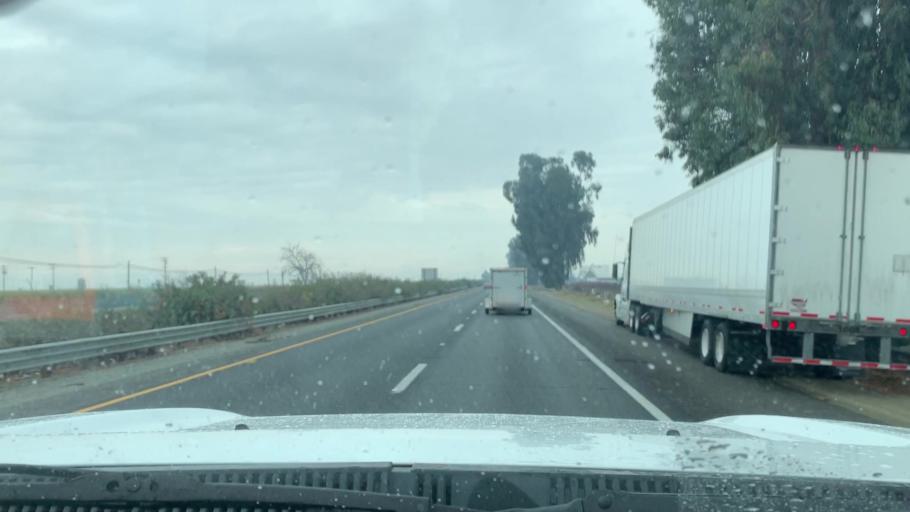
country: US
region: California
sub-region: Kern County
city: Delano
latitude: 35.8100
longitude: -119.2568
